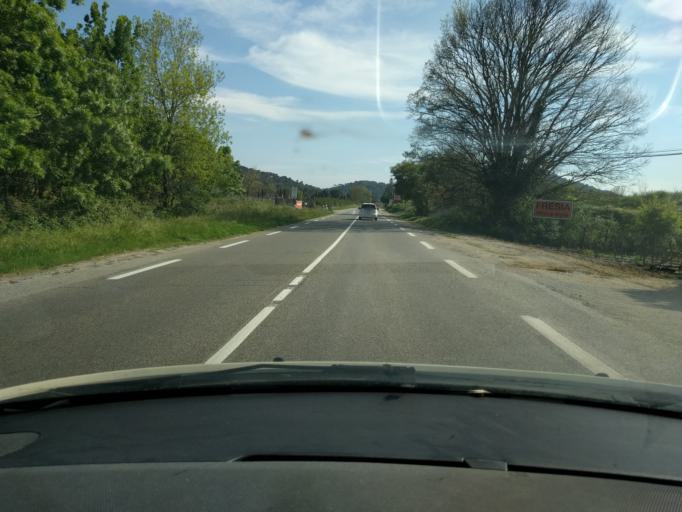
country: FR
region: Provence-Alpes-Cote d'Azur
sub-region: Departement du Var
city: La Crau
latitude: 43.1775
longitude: 6.1177
